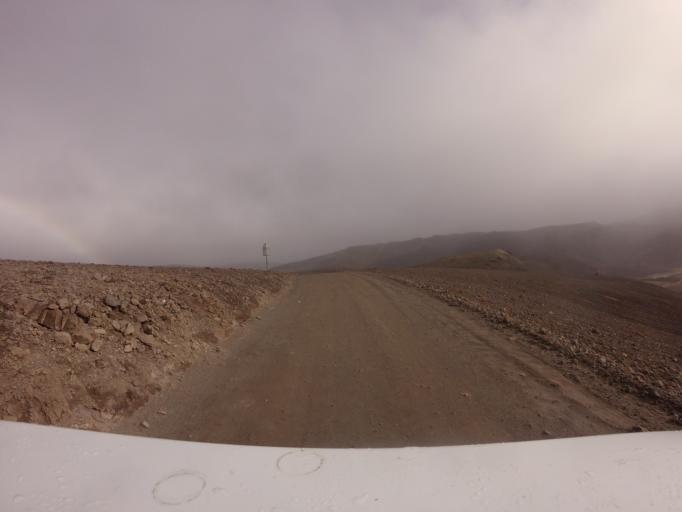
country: IS
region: South
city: Vestmannaeyjar
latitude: 63.9802
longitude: -18.8936
